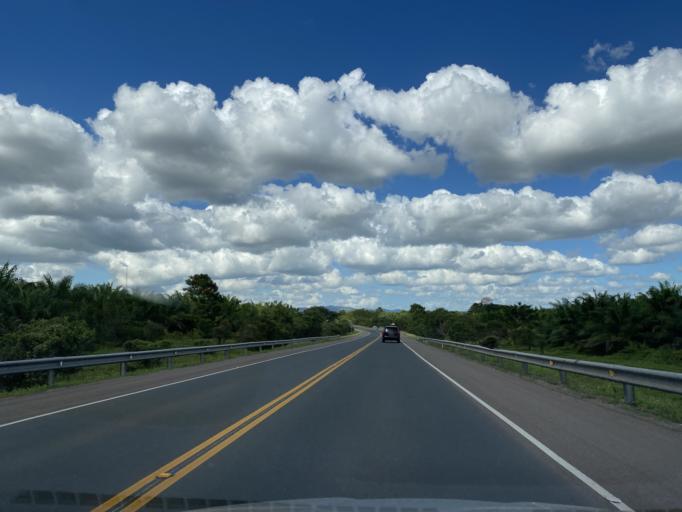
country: DO
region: Monte Plata
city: Monte Plata
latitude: 18.7280
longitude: -69.7609
